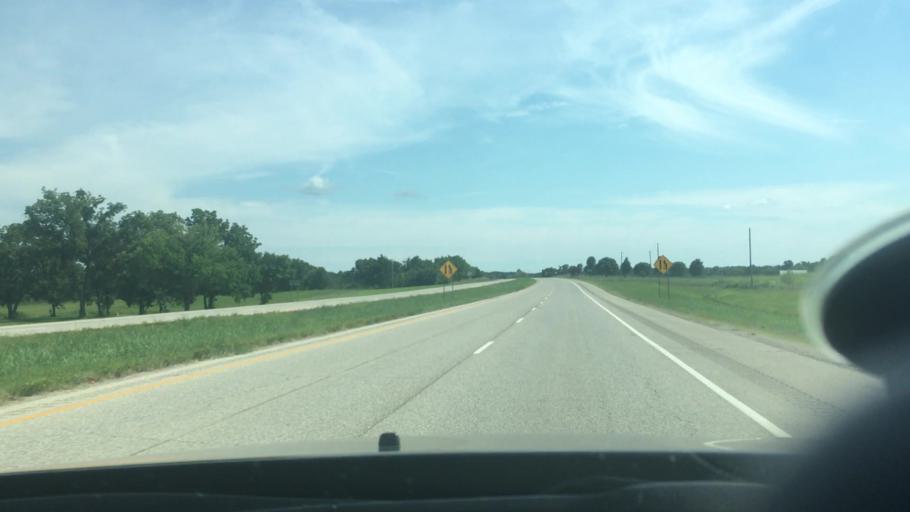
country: US
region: Oklahoma
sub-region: Seminole County
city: Seminole
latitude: 35.1877
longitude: -96.6752
